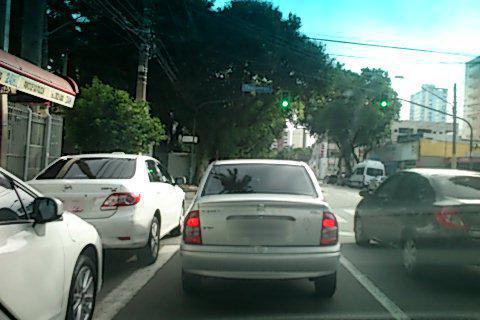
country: BR
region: Sao Paulo
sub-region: Sao Jose Dos Campos
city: Sao Jose dos Campos
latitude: -23.1969
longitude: -45.8945
